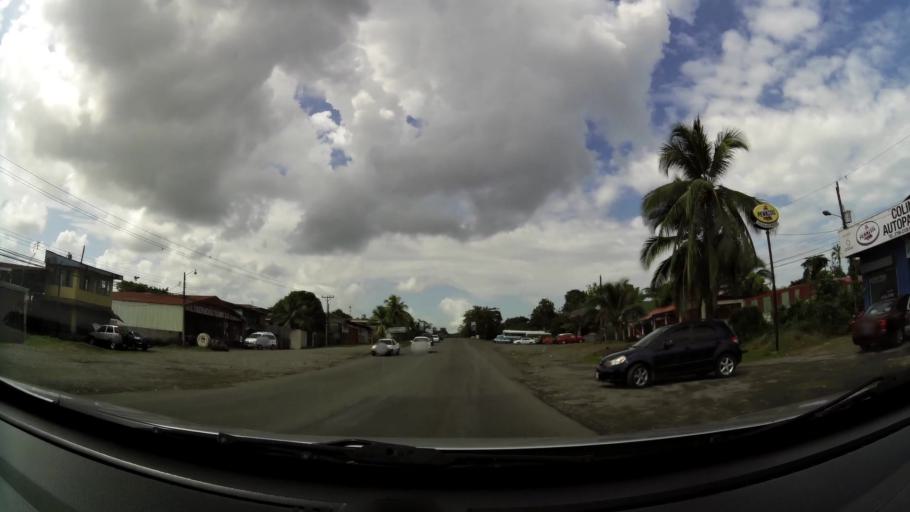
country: CR
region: Limon
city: Limon
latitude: 9.9854
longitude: -83.0495
